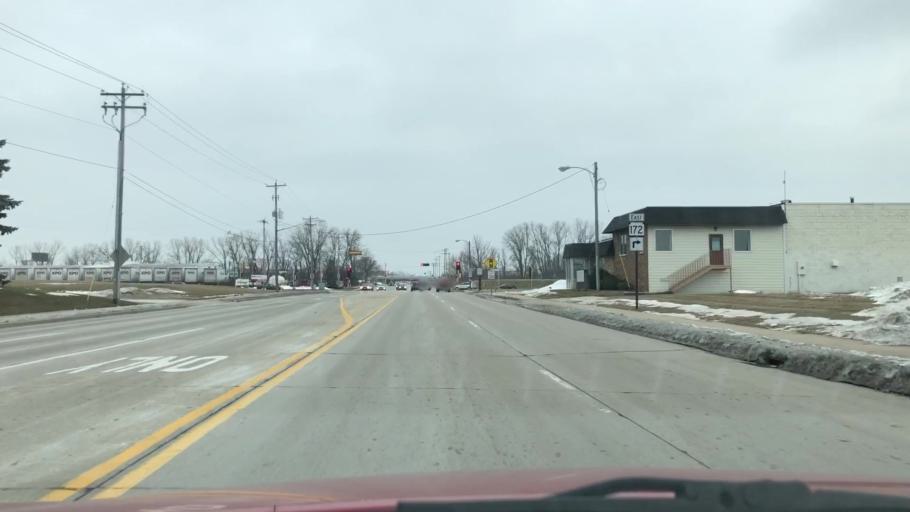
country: US
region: Wisconsin
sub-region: Brown County
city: Ashwaubenon
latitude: 44.4747
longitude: -88.0699
